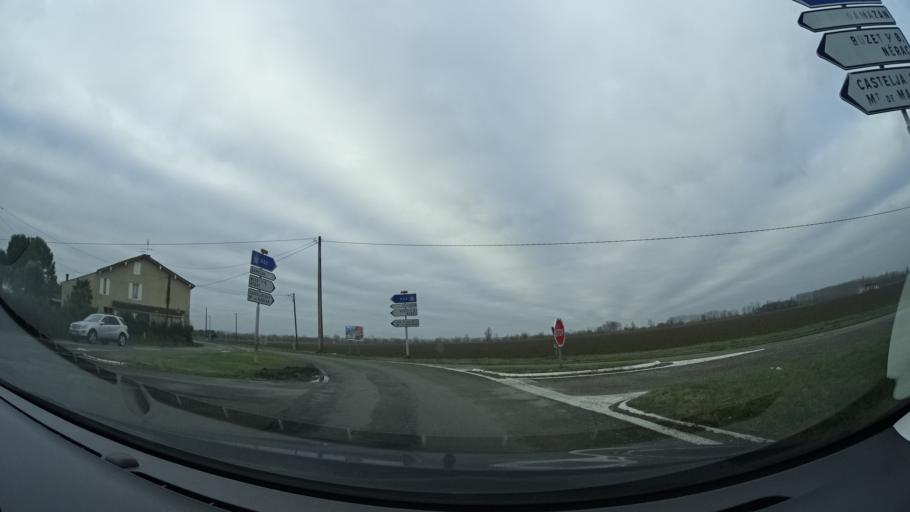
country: FR
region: Aquitaine
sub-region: Departement du Lot-et-Garonne
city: Aiguillon
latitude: 44.2964
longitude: 0.3326
